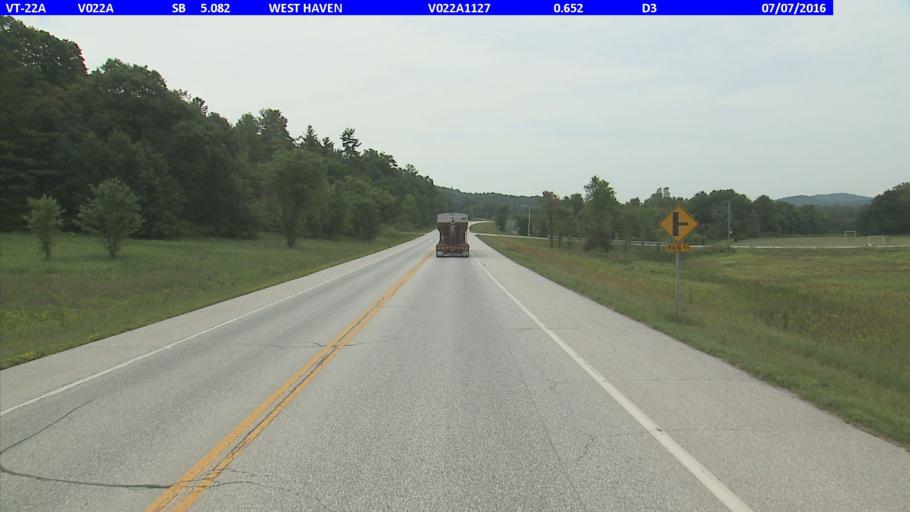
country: US
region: Vermont
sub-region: Rutland County
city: Fair Haven
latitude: 43.6375
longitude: -73.2976
